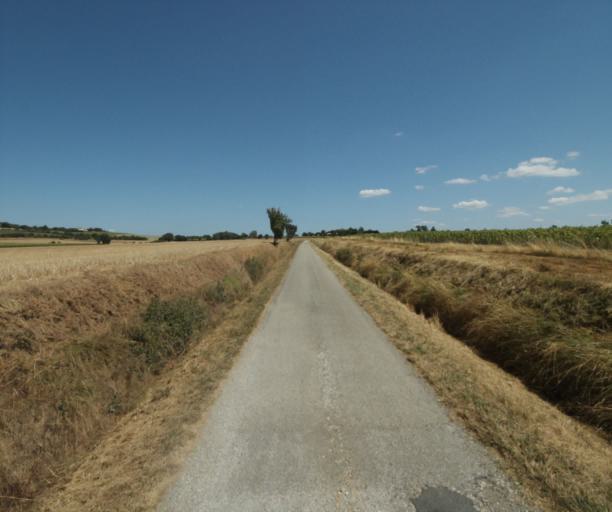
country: FR
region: Midi-Pyrenees
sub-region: Departement de la Haute-Garonne
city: Saint-Felix-Lauragais
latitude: 43.4844
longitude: 1.8873
